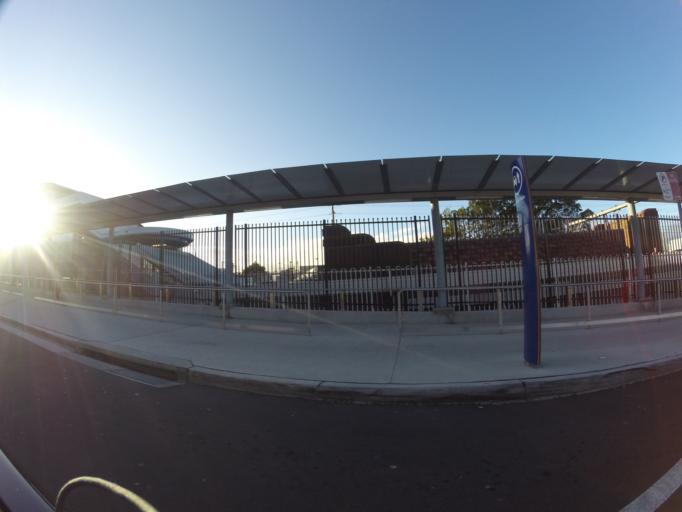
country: AU
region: New South Wales
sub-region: Sutherland Shire
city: Kirrawee
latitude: -34.0316
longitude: 151.0570
